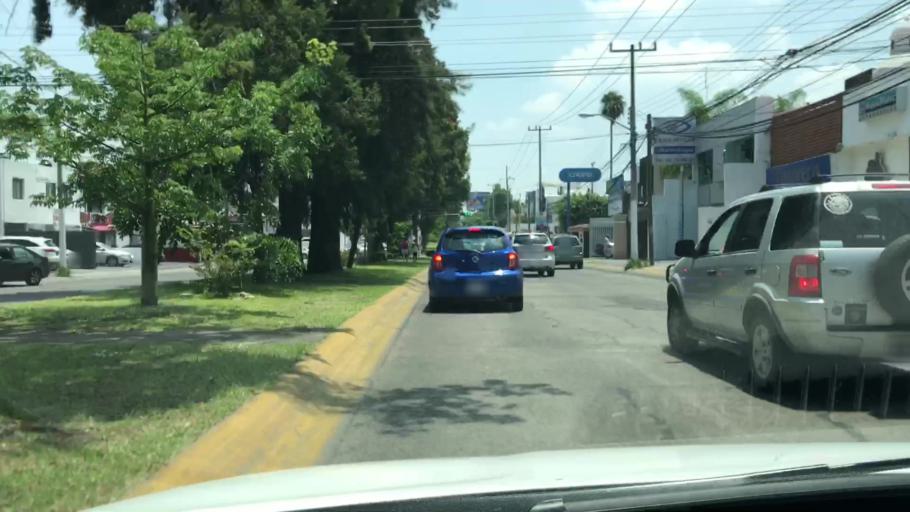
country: MX
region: Jalisco
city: Guadalajara
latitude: 20.6706
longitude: -103.4311
